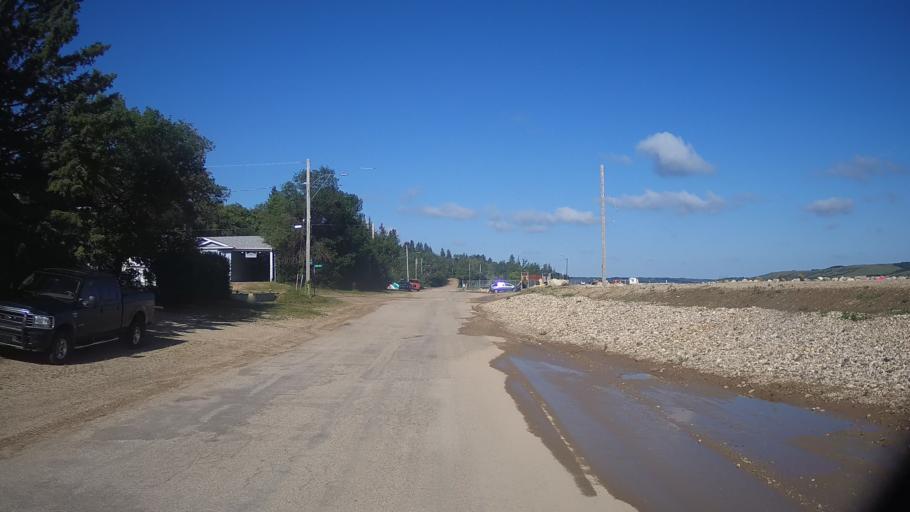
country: CA
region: Saskatchewan
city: Watrous
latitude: 51.7214
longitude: -105.4481
